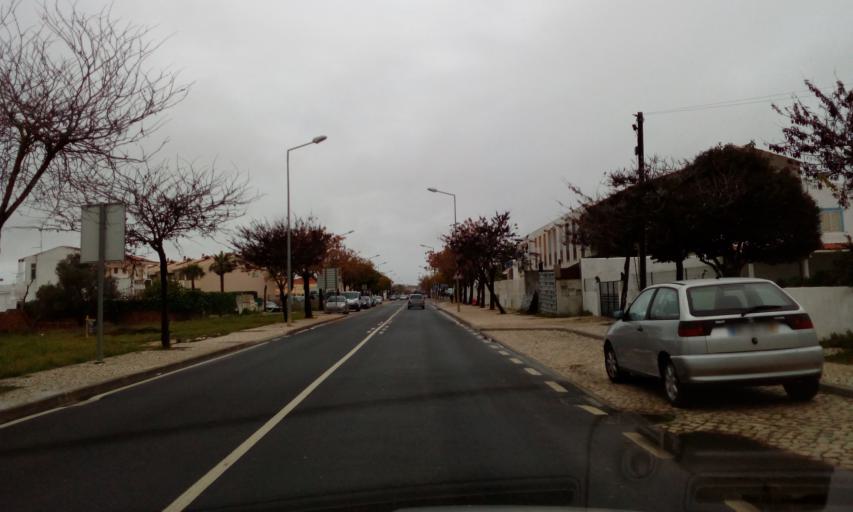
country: PT
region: Faro
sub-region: Albufeira
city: Ferreiras
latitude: 37.1256
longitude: -8.2338
